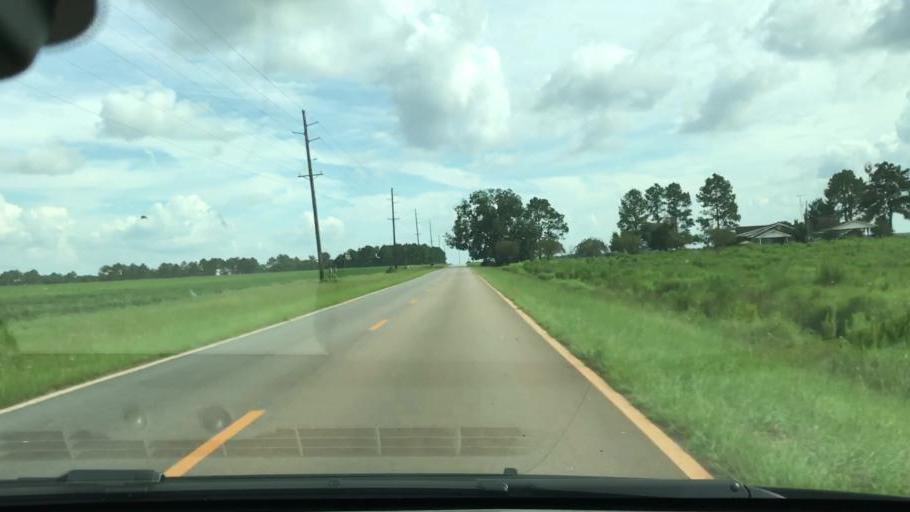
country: US
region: Georgia
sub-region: Clay County
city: Fort Gaines
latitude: 31.5388
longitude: -84.9613
